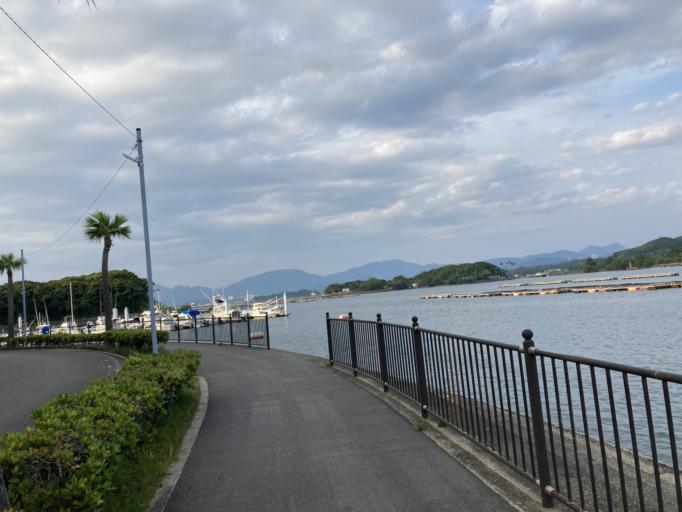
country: JP
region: Wakayama
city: Tanabe
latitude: 33.6829
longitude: 135.3605
